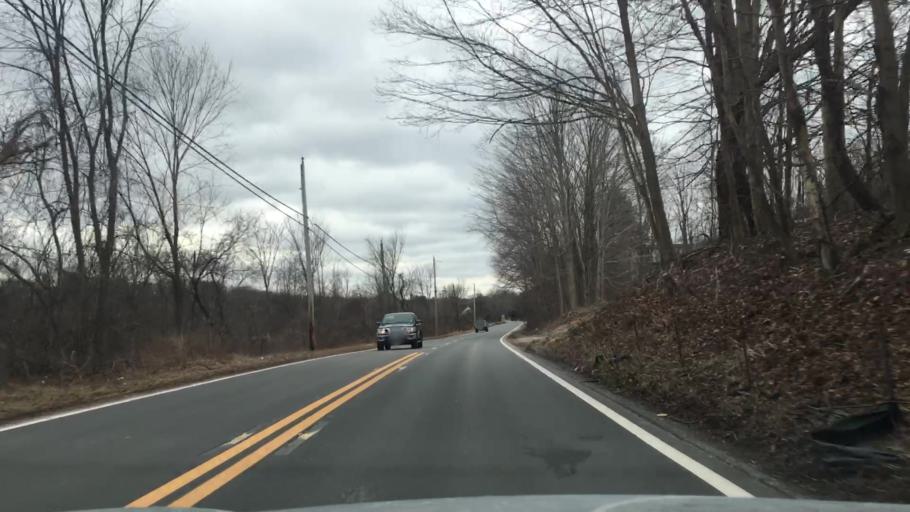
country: US
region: Connecticut
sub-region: Hartford County
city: North Granby
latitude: 42.0097
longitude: -72.7953
